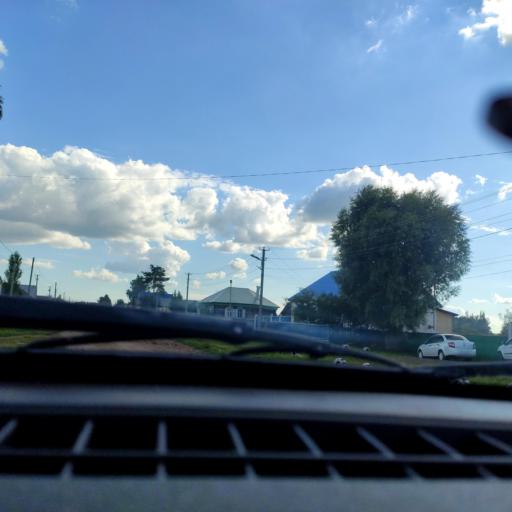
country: RU
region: Bashkortostan
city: Mikhaylovka
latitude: 54.9520
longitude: 55.7664
